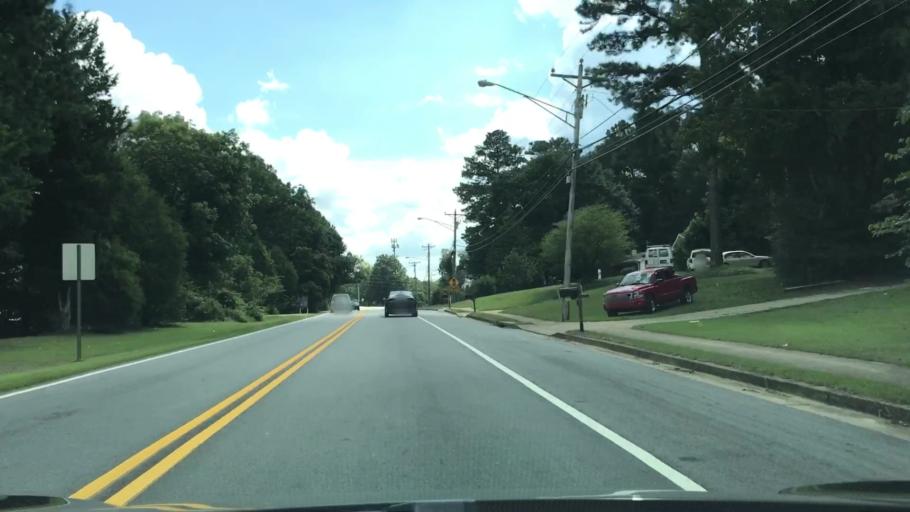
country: US
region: Georgia
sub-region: Gwinnett County
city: Snellville
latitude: 33.8904
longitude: -84.0644
